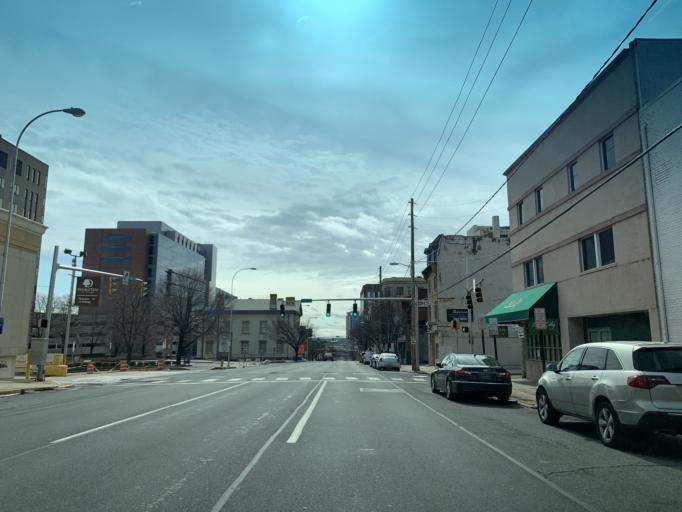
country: US
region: Delaware
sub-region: New Castle County
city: Wilmington
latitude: 39.7426
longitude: -75.5487
